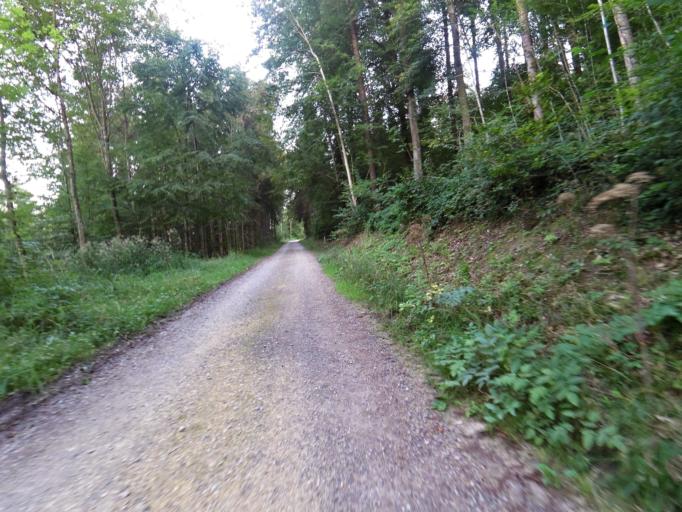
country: CH
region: Thurgau
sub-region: Weinfelden District
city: Wigoltingen
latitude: 47.5779
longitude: 9.0142
